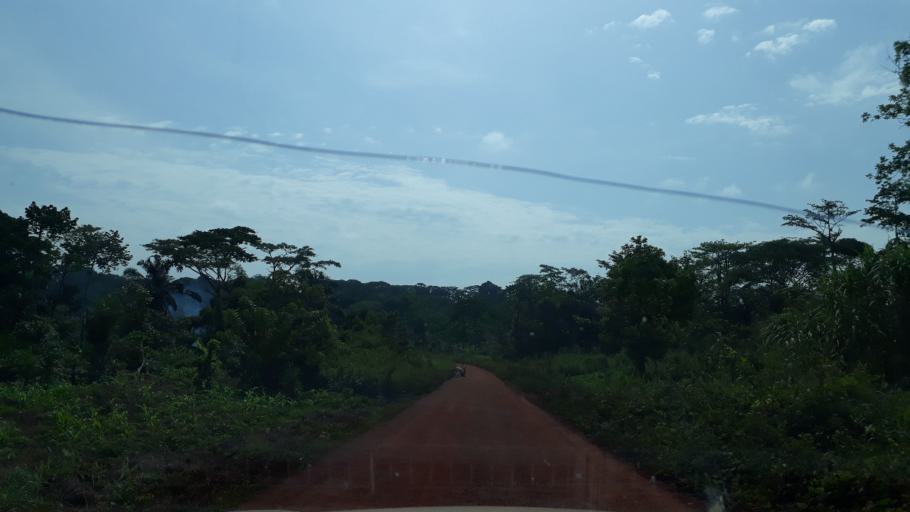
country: CD
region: Eastern Province
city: Wamba
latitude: 1.4091
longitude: 28.0895
